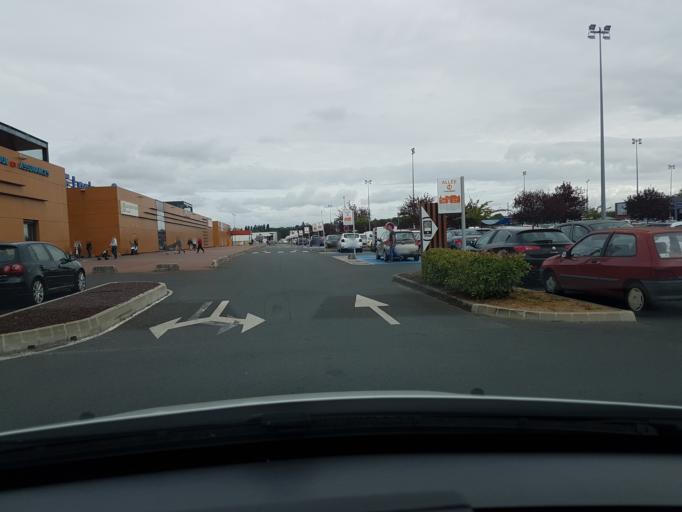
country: FR
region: Centre
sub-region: Departement d'Indre-et-Loire
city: La Ville-aux-Dames
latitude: 47.3942
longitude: 0.7867
